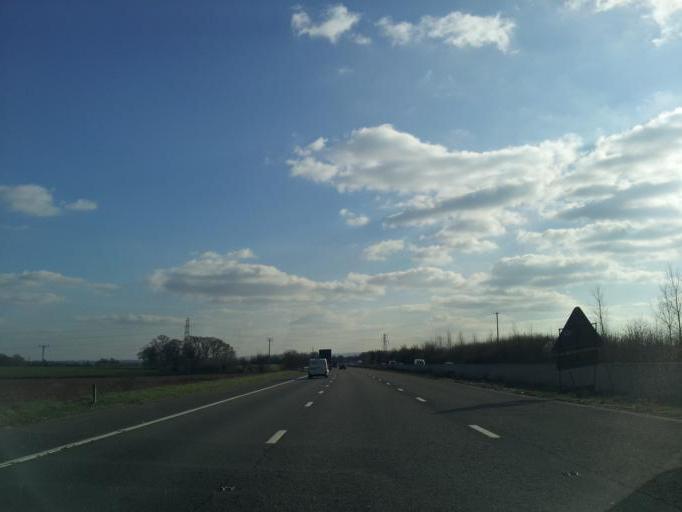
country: GB
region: England
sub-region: Somerset
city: North Petherton
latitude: 51.0889
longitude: -3.0043
